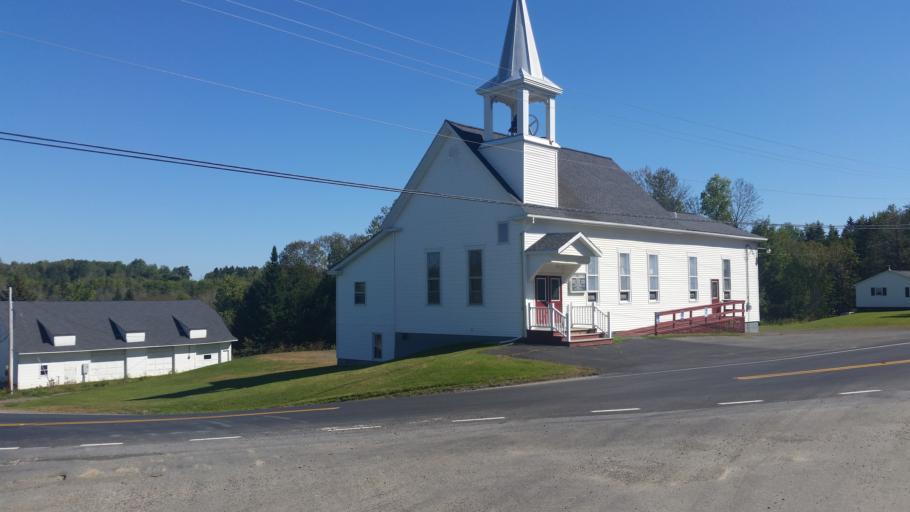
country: US
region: Maine
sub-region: Aroostook County
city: Caribou
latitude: 46.8446
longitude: -68.1974
